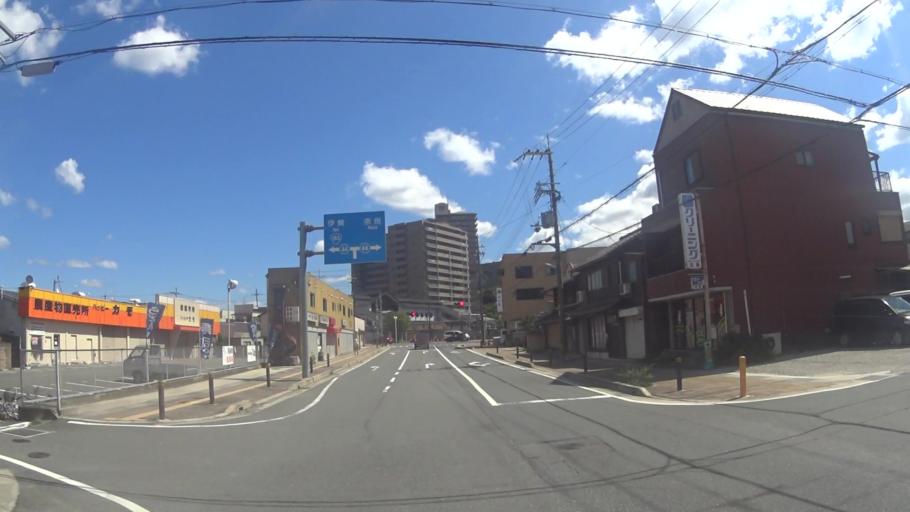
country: JP
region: Nara
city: Nara-shi
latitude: 34.7527
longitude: 135.8681
